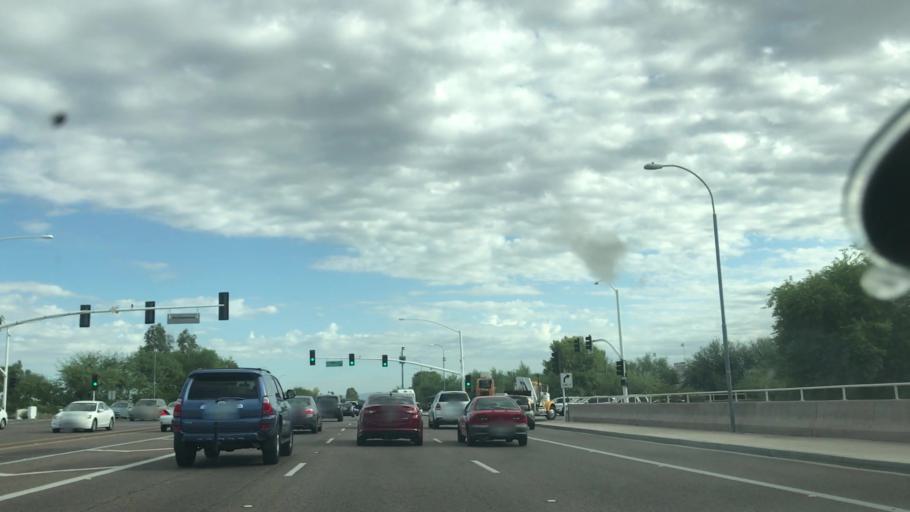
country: US
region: Arizona
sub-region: Maricopa County
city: Scottsdale
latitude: 33.5232
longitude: -111.9087
